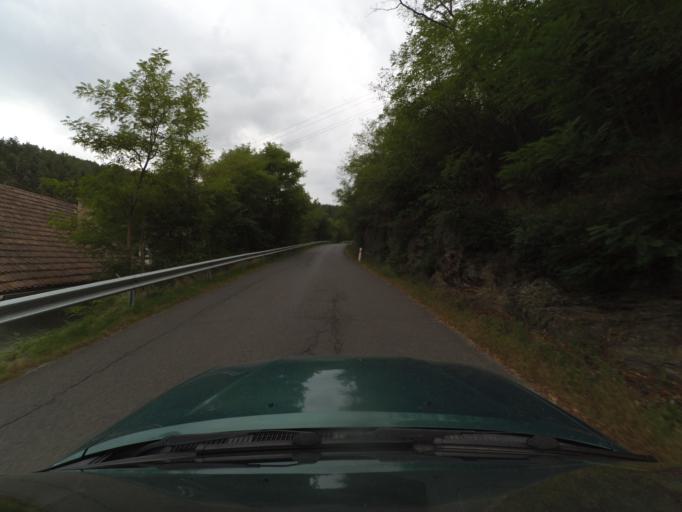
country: CZ
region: Plzensky
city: Kralovice
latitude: 49.9159
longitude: 13.5182
